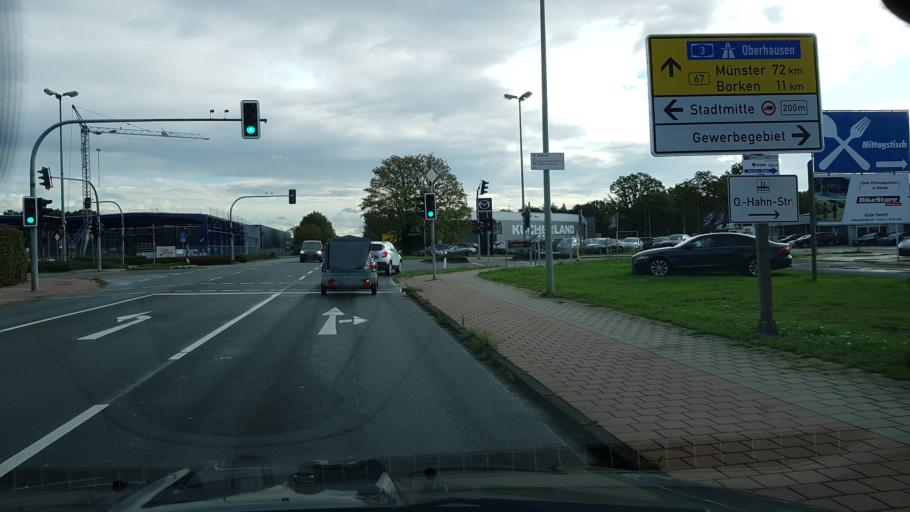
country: DE
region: North Rhine-Westphalia
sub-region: Regierungsbezirk Munster
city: Rhede
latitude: 51.8327
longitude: 6.7109
